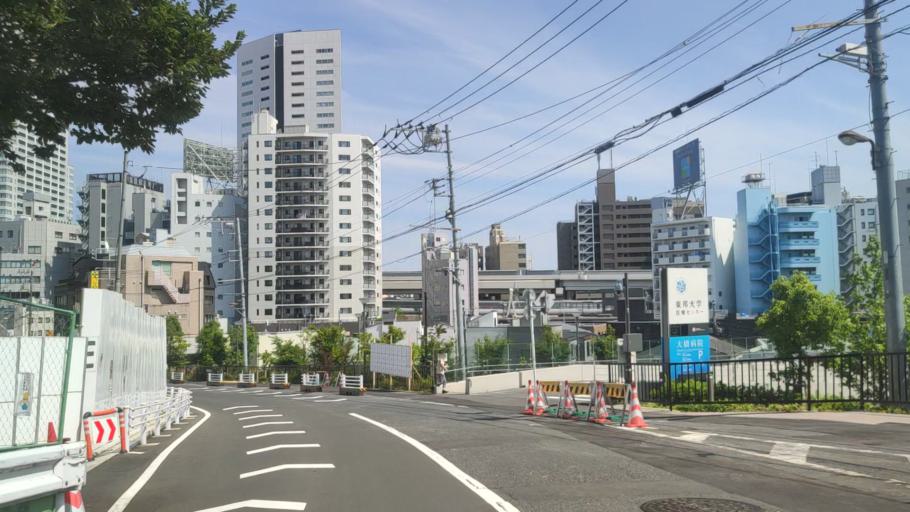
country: JP
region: Tokyo
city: Tokyo
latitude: 35.6528
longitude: 139.6843
